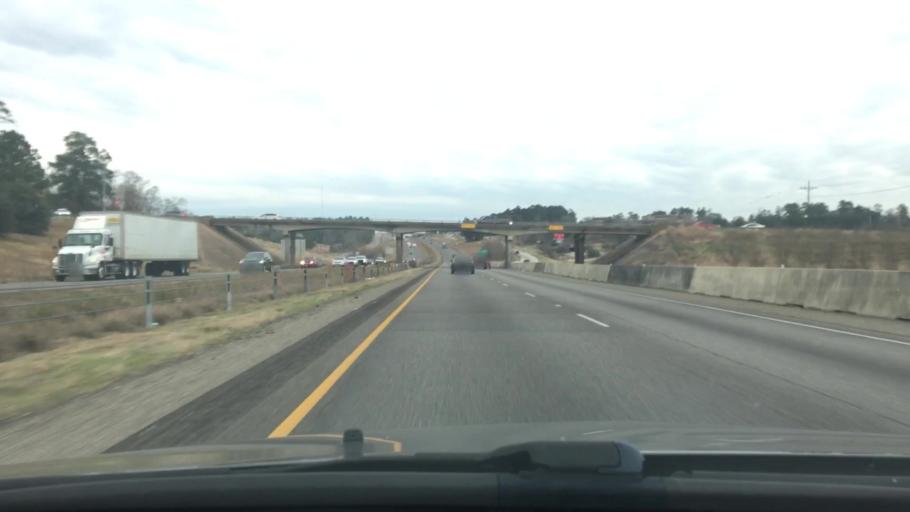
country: US
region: Texas
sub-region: Walker County
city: Huntsville
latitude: 30.7062
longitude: -95.5619
